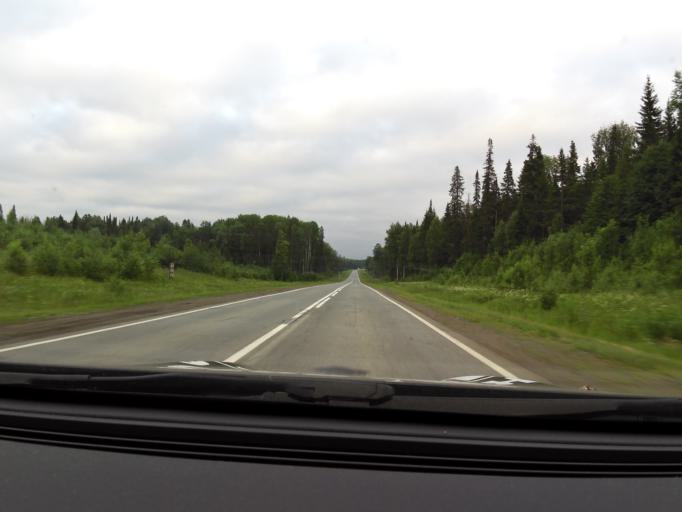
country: RU
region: Perm
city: Zyukayka
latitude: 58.3710
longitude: 54.6535
